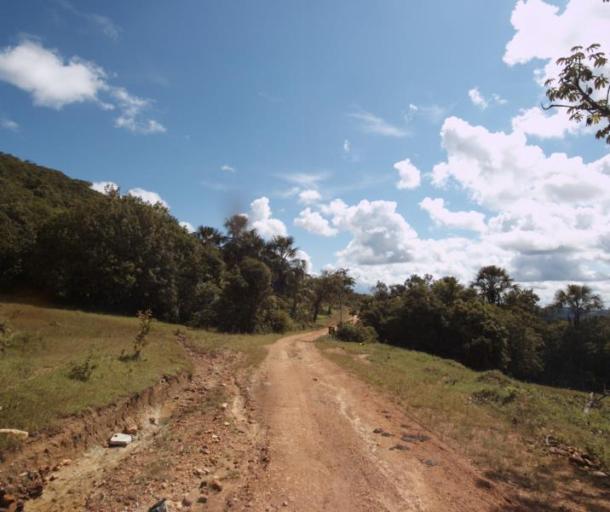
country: BR
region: Goias
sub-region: Pirenopolis
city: Pirenopolis
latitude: -15.7806
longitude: -48.9644
